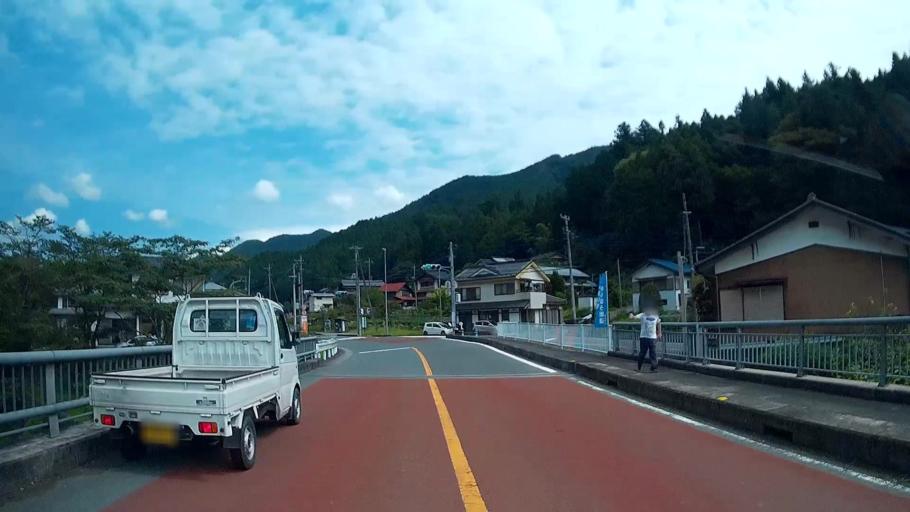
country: JP
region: Tokyo
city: Ome
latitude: 35.8659
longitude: 139.1869
